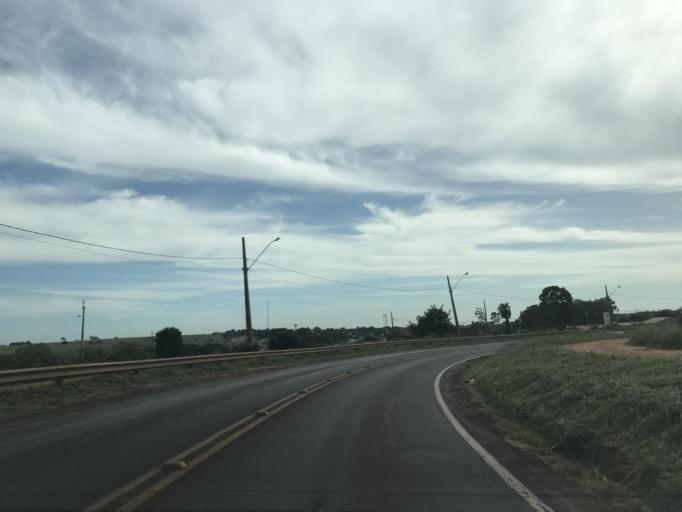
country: BR
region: Parana
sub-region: Paranavai
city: Nova Aurora
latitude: -22.9438
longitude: -52.6962
